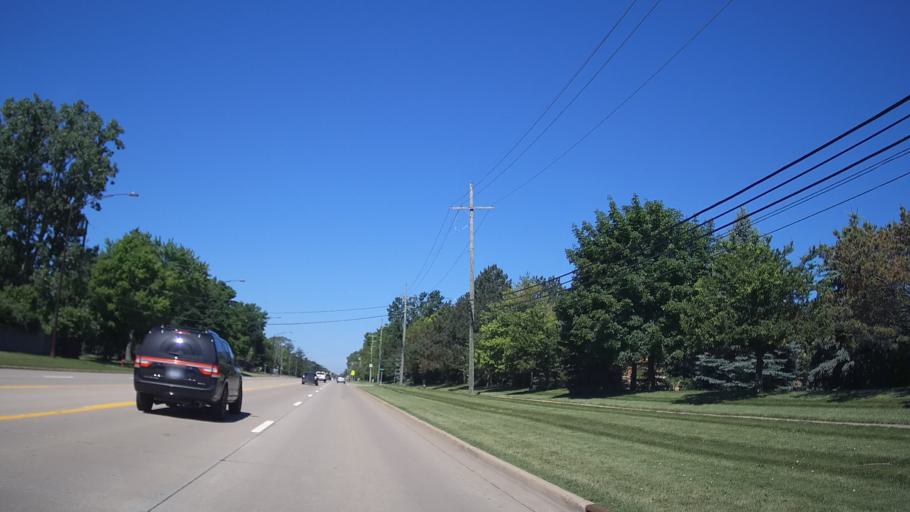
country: US
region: Michigan
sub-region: Oakland County
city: Troy
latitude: 42.5928
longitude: -83.1006
